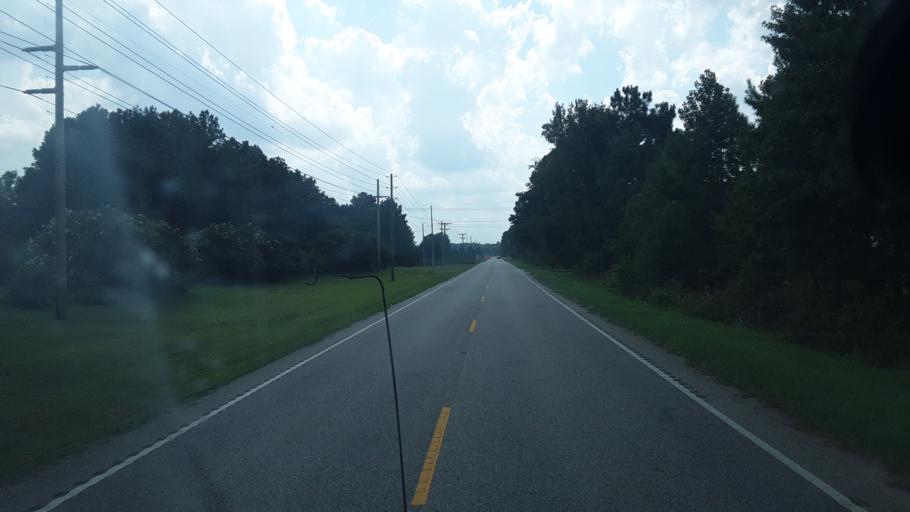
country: US
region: South Carolina
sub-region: Sumter County
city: Sumter
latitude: 33.9663
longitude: -80.3653
